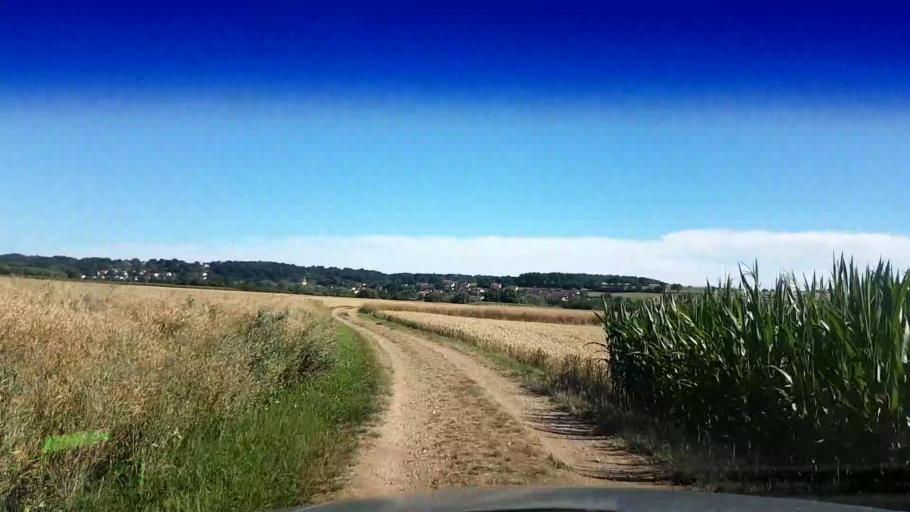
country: DE
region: Bavaria
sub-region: Upper Franconia
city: Viereth-Trunstadt
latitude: 49.9329
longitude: 10.7631
